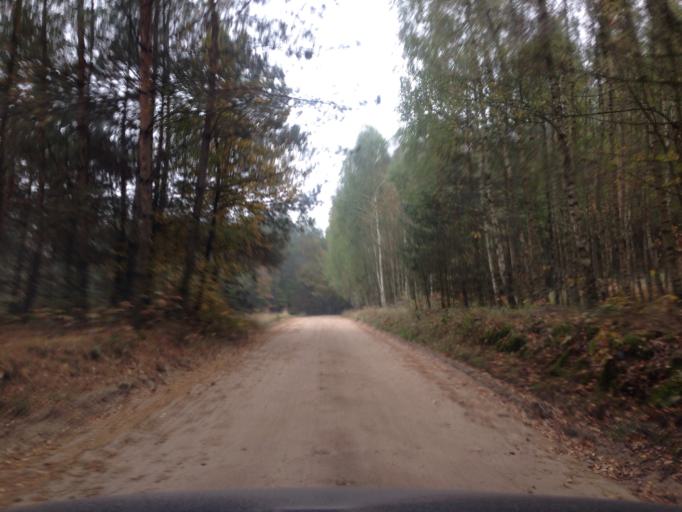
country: PL
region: Kujawsko-Pomorskie
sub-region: Powiat brodnicki
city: Gorzno
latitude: 53.2766
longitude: 19.7046
